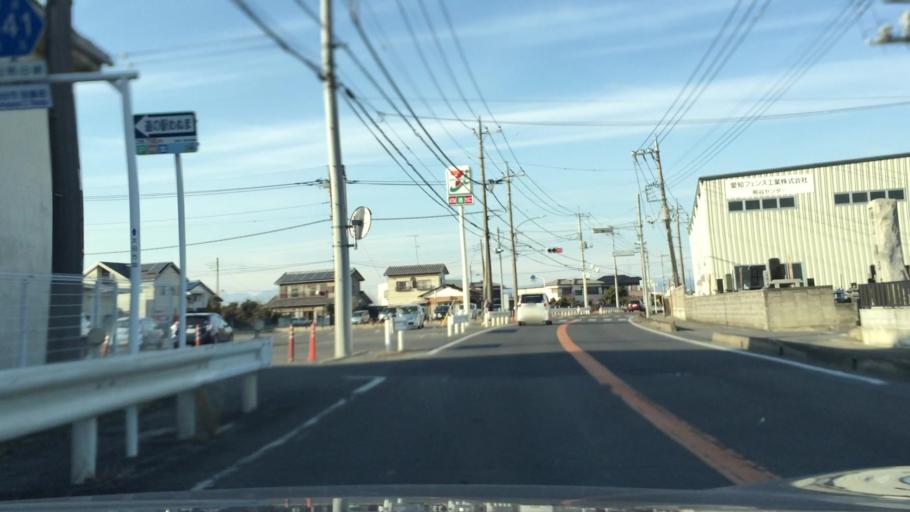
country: JP
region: Saitama
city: Menuma
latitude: 36.2142
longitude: 139.3777
